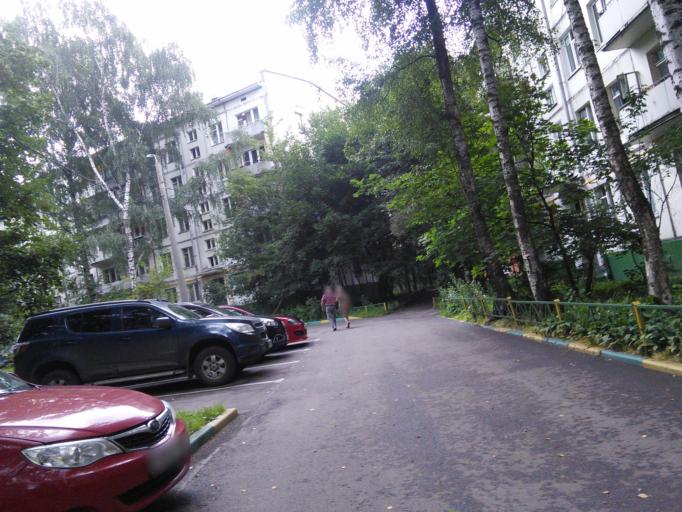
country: RU
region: Moskovskaya
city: Bogorodskoye
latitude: 55.7956
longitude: 37.7265
